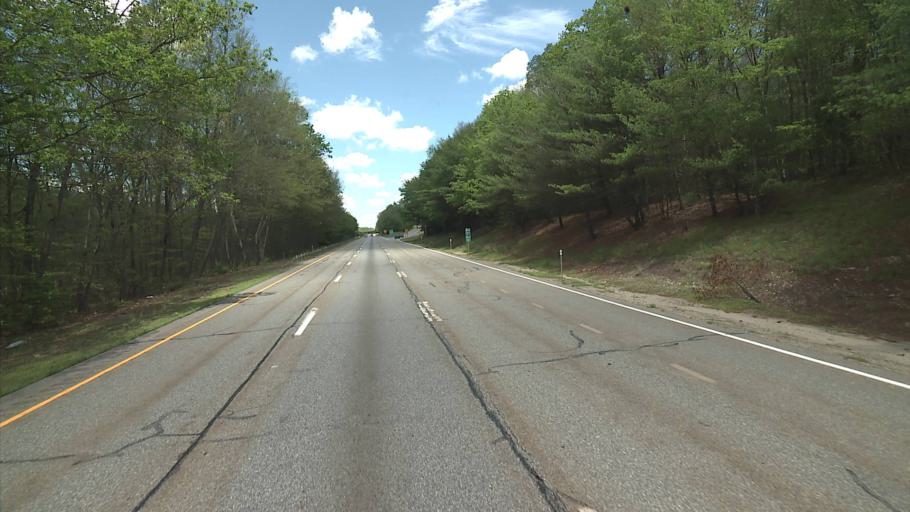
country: US
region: Connecticut
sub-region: Windham County
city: Thompson
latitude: 41.9595
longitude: -71.8760
